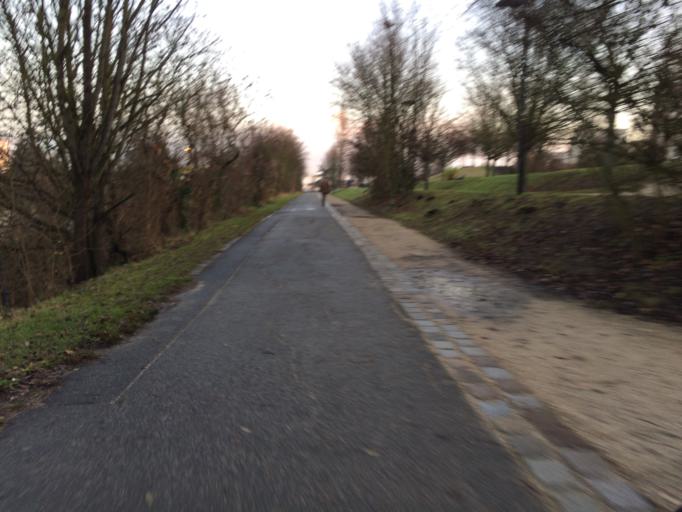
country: FR
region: Ile-de-France
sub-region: Departement des Hauts-de-Seine
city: Fontenay-aux-Roses
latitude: 48.7961
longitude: 2.2952
